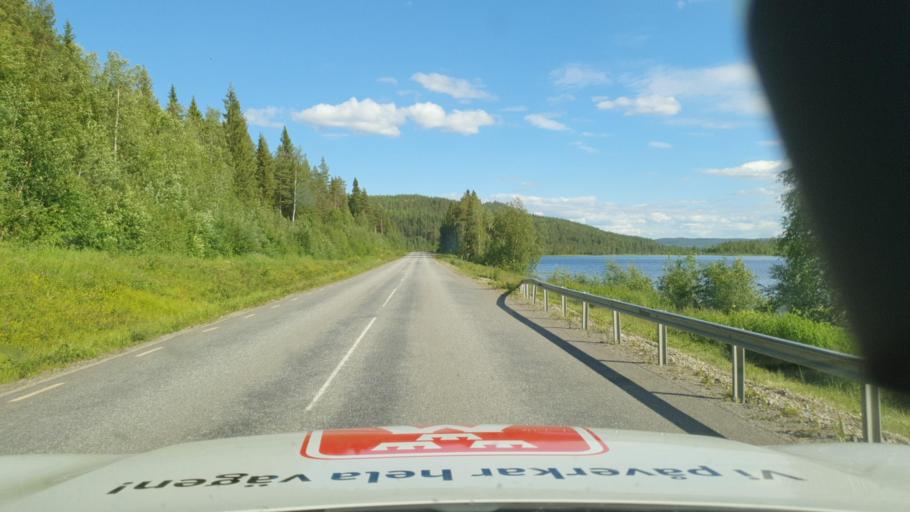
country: SE
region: Vaesterbotten
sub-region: Norsjo Kommun
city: Norsjoe
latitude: 64.8572
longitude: 19.7351
